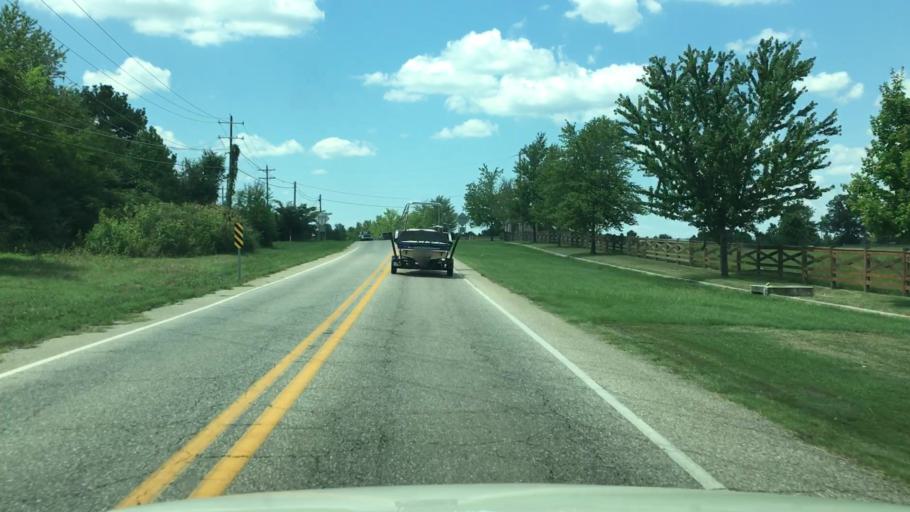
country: US
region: Arkansas
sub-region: Garland County
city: Lake Hamilton
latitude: 34.4062
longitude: -93.0909
